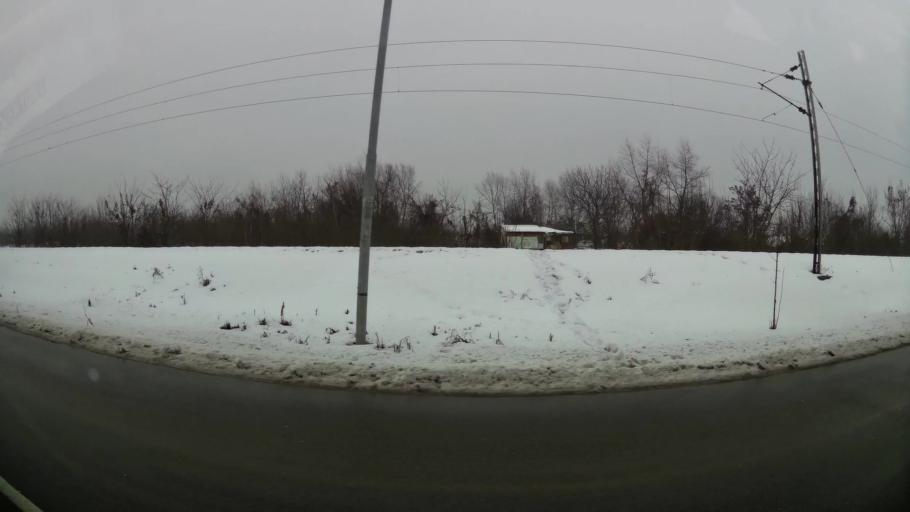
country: RS
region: Central Serbia
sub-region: Belgrade
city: Zemun
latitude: 44.8440
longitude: 20.3493
